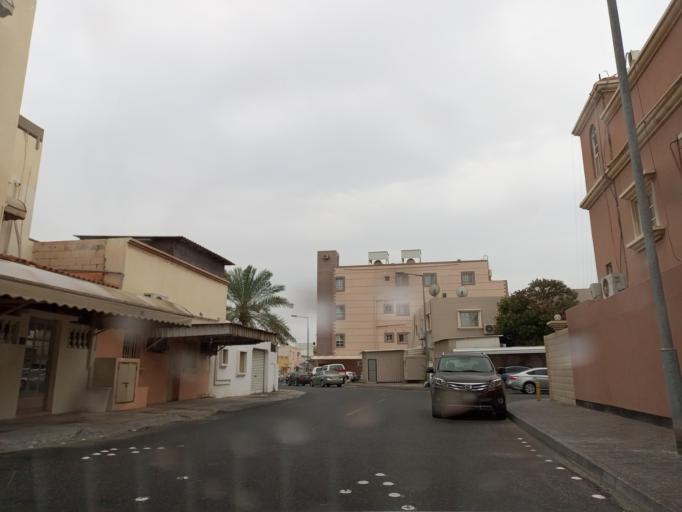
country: BH
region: Muharraq
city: Al Muharraq
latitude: 26.2593
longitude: 50.6338
